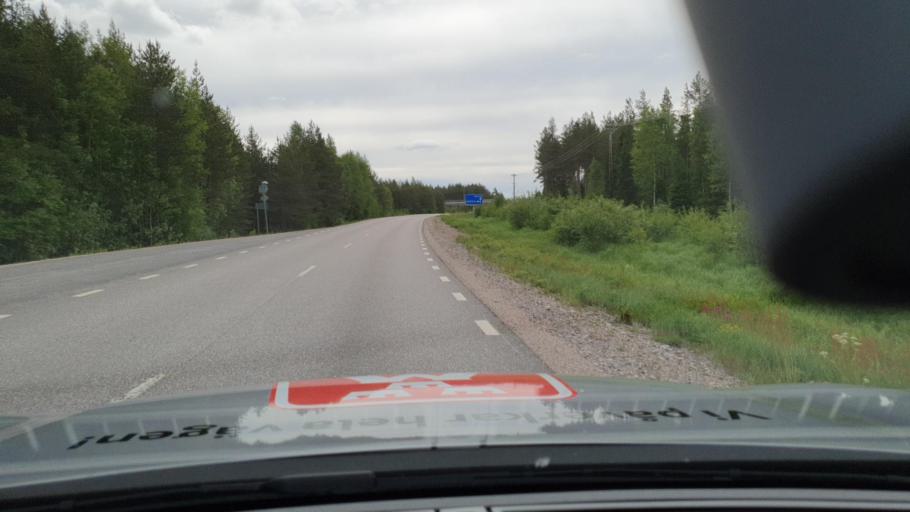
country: SE
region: Norrbotten
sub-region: Kalix Kommun
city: Kalix
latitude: 65.8765
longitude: 23.4854
